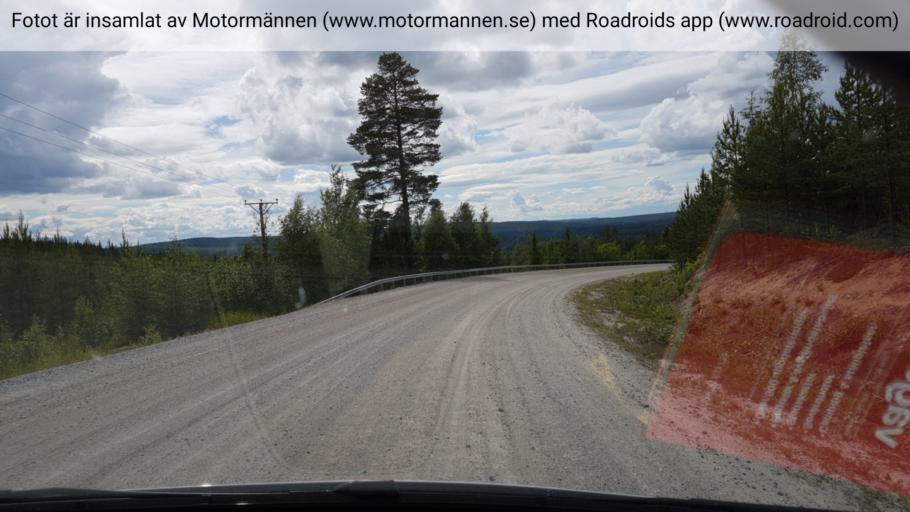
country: SE
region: Vaesternorrland
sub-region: Solleftea Kommun
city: Solleftea
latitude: 63.3521
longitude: 17.4881
